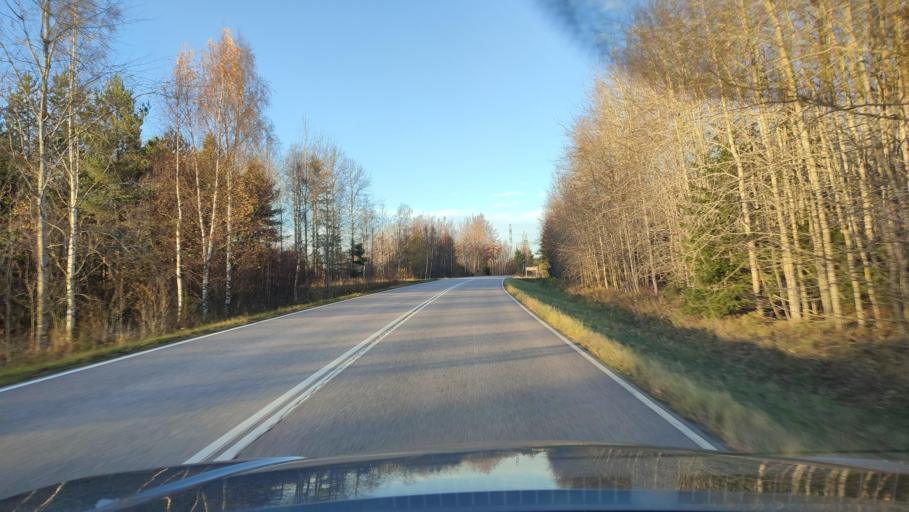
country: FI
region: Ostrobothnia
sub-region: Sydosterbotten
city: Kristinestad
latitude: 62.2883
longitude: 21.3775
